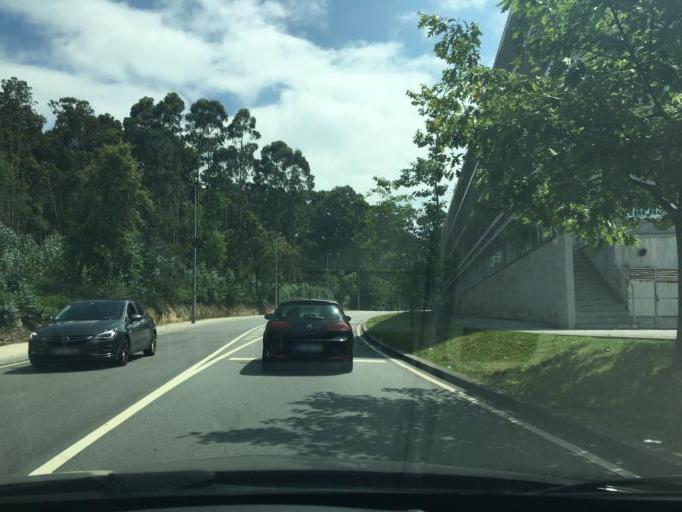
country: PT
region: Porto
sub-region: Maia
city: Gemunde
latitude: 41.2551
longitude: -8.6390
